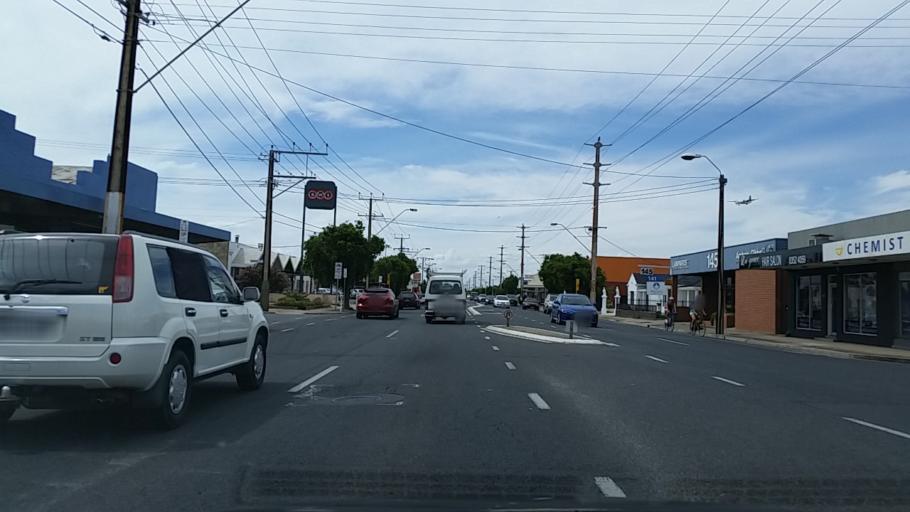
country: AU
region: South Australia
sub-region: City of West Torrens
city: Plympton
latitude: -34.9383
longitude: 138.5529
